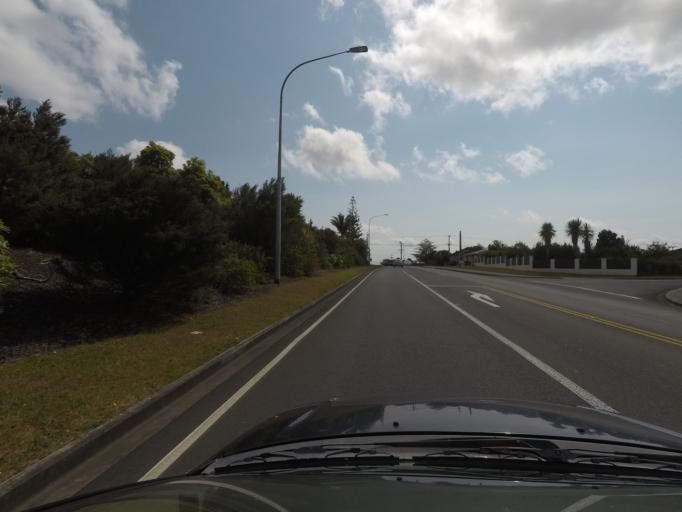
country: NZ
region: Northland
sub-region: Whangarei
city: Whangarei
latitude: -35.6886
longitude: 174.3226
